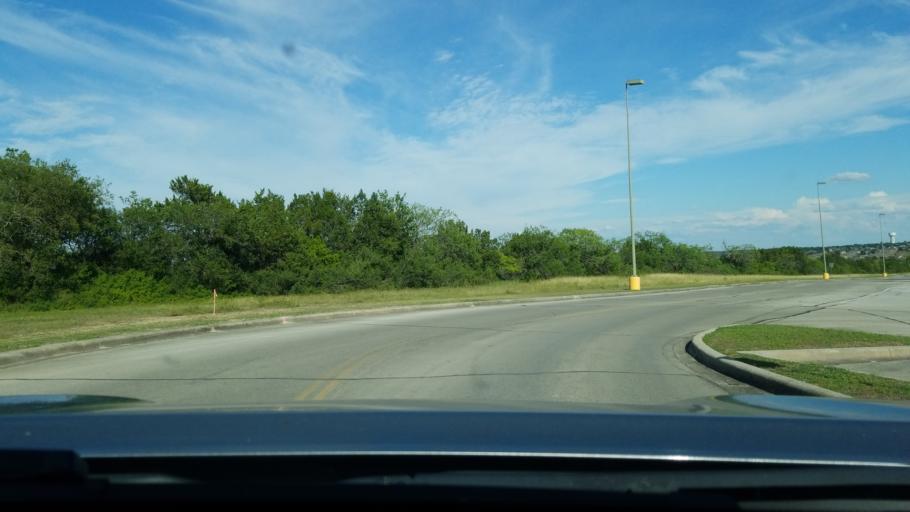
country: US
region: Texas
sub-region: Bexar County
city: Live Oak
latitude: 29.5983
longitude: -98.3484
